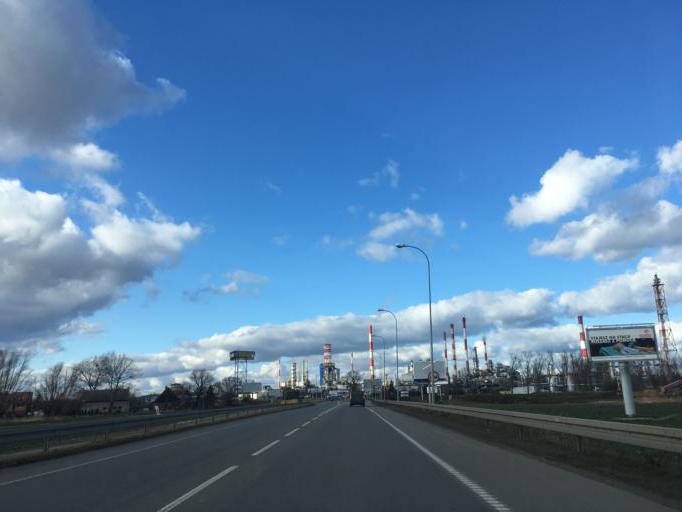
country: PL
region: Pomeranian Voivodeship
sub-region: Gdansk
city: Gdansk
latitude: 54.3361
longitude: 18.7404
